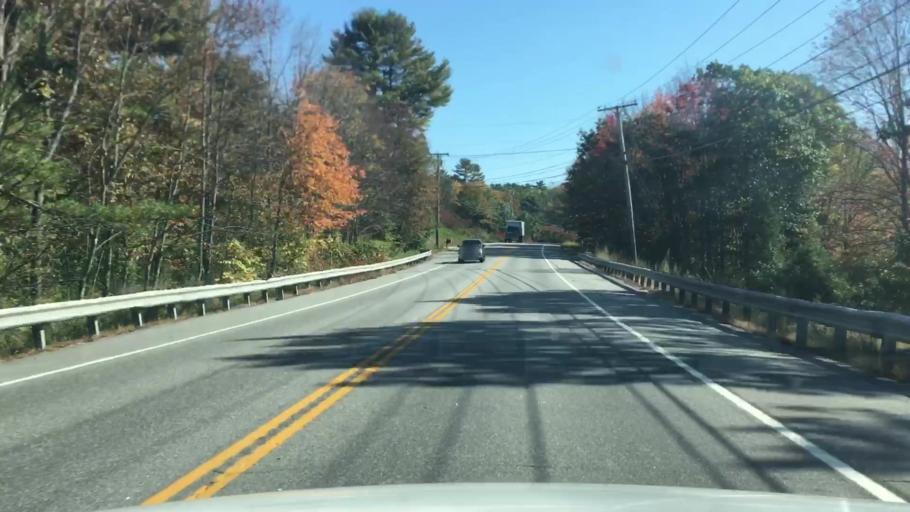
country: US
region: Maine
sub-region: Androscoggin County
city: Lisbon Falls
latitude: 43.9849
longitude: -70.0378
